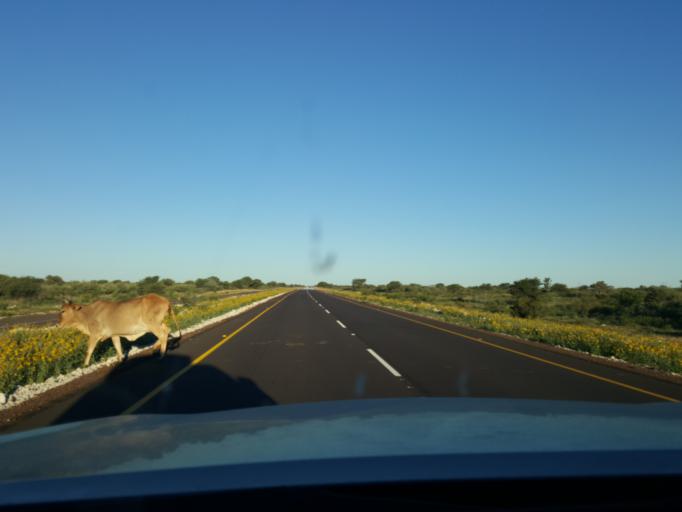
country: BW
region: Southern
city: Sekoma
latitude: -24.4478
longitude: 23.7671
